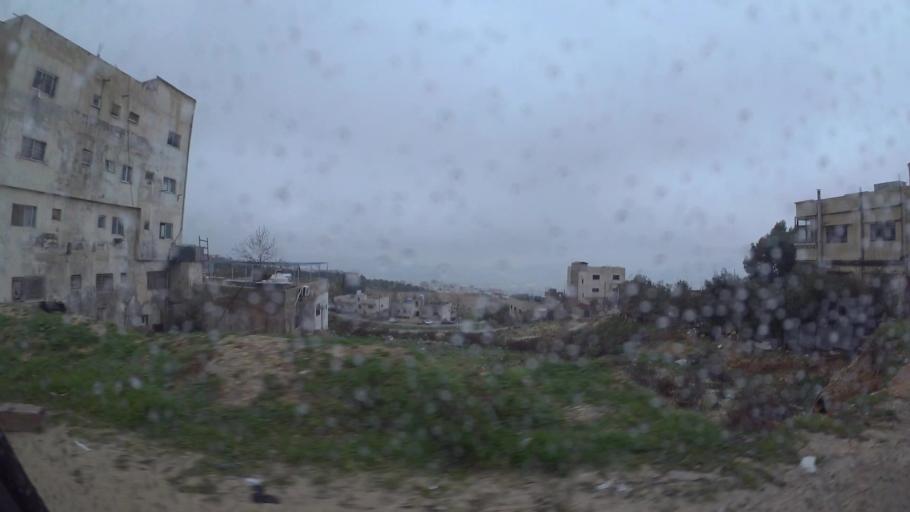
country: JO
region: Amman
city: Al Jubayhah
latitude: 32.0362
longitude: 35.8503
